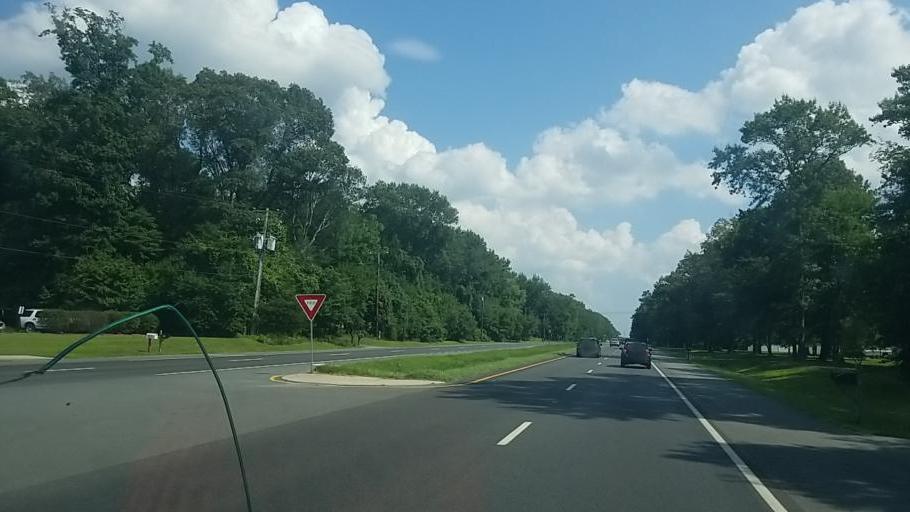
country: US
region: Delaware
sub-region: Sussex County
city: Millsboro
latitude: 38.5612
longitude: -75.2741
